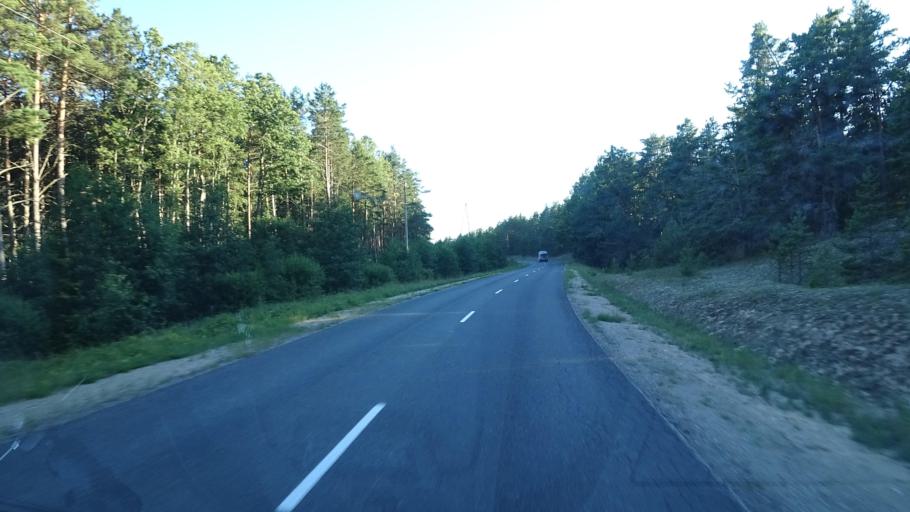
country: LV
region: Dundaga
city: Dundaga
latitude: 57.7212
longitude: 22.5761
